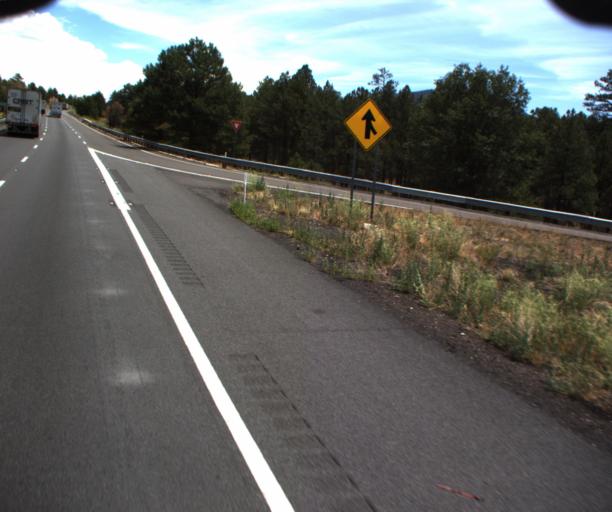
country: US
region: Arizona
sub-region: Coconino County
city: Williams
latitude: 35.2198
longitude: -112.2774
